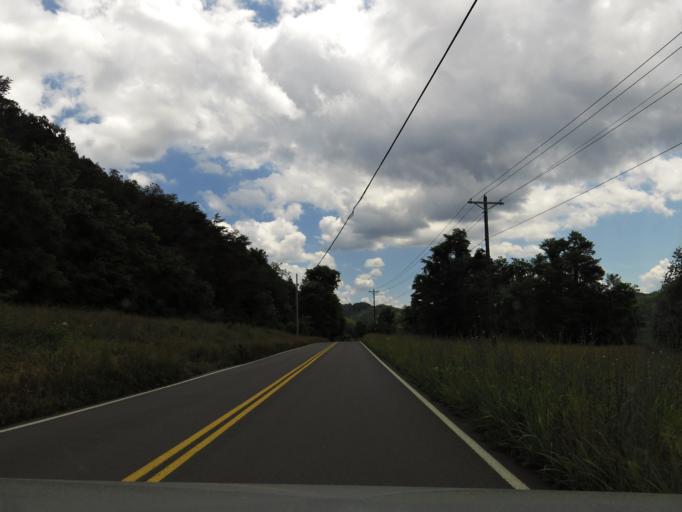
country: US
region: Tennessee
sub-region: Loudon County
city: Greenback
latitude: 35.5456
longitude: -84.0750
